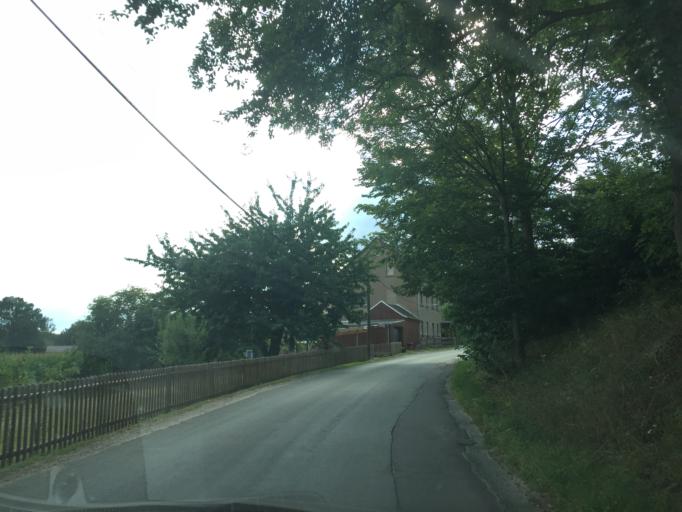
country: DE
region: Thuringia
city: Altenburg
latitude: 50.9626
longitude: 12.4532
